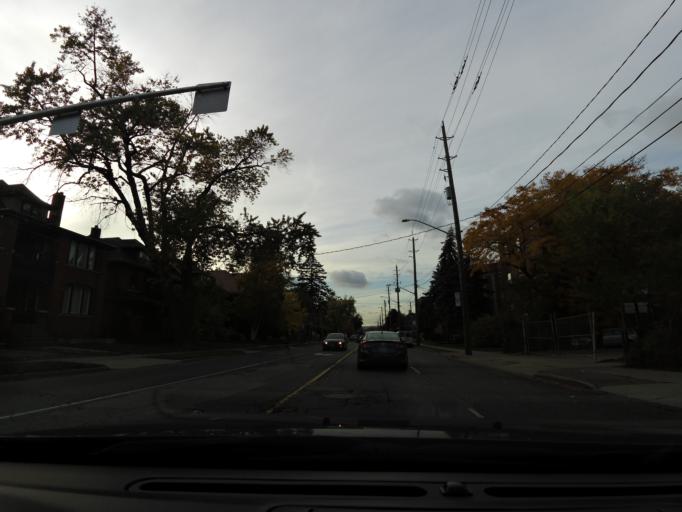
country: CA
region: Ontario
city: Hamilton
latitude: 43.2513
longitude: -79.8937
